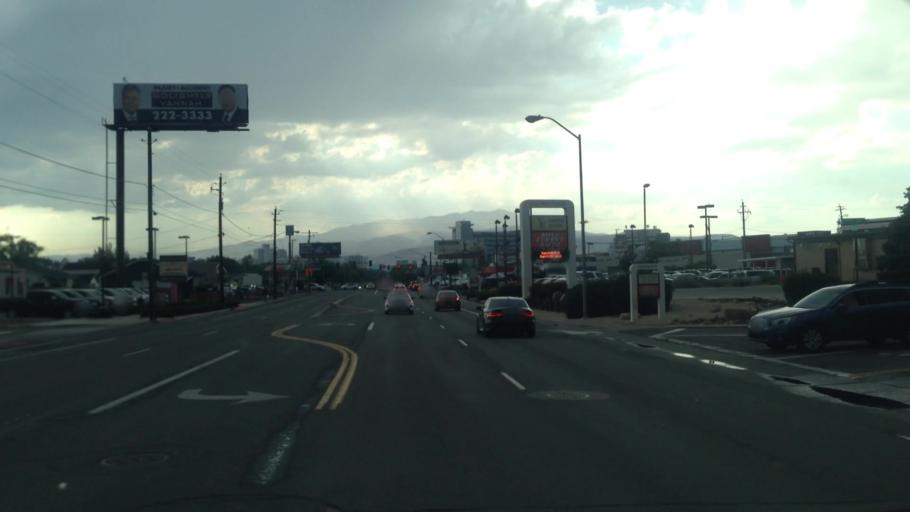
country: US
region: Nevada
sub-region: Washoe County
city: Reno
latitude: 39.5210
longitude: -119.7866
